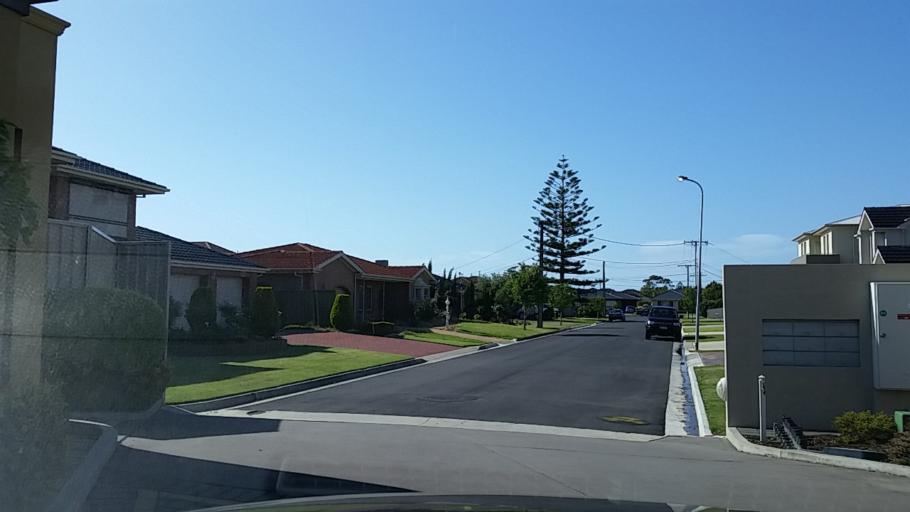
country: AU
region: South Australia
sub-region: Charles Sturt
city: Henley Beach
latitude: -34.9149
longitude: 138.5089
